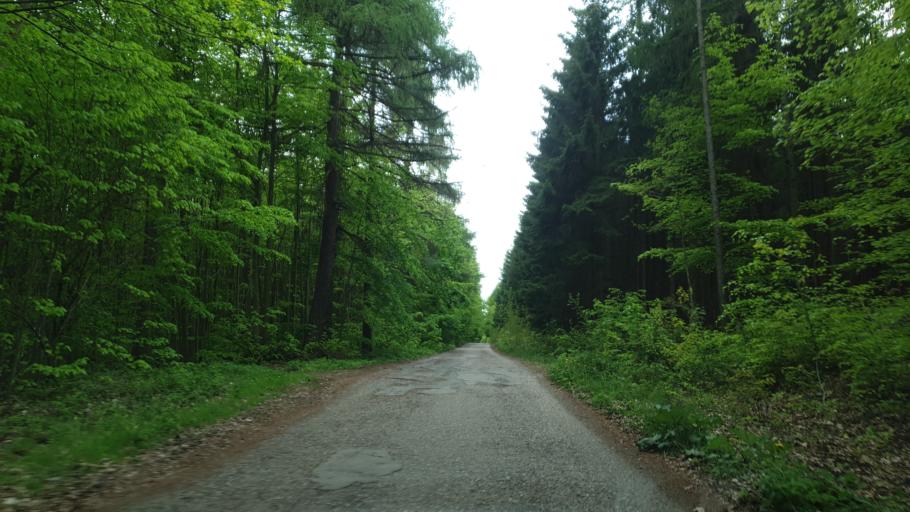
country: DE
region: Saxony
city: Hohndorf
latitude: 50.7200
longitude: 12.6649
